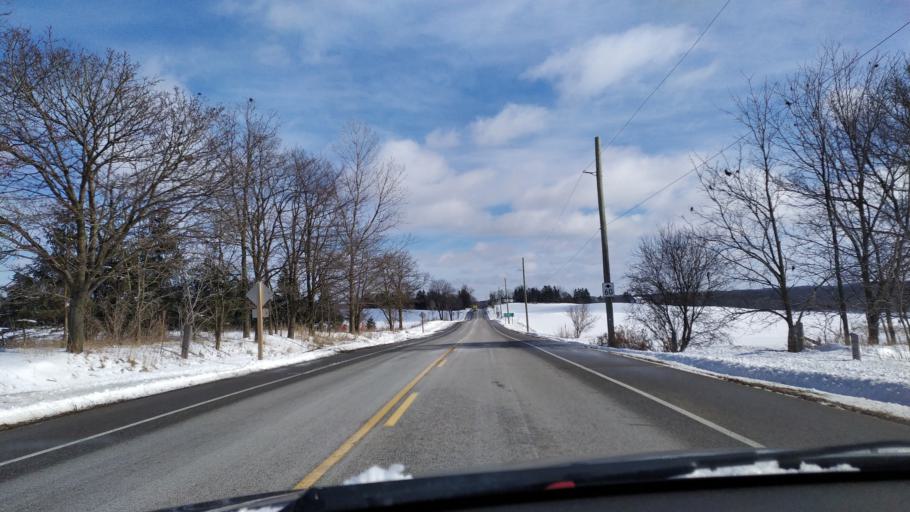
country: CA
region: Ontario
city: Waterloo
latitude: 43.4744
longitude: -80.6999
